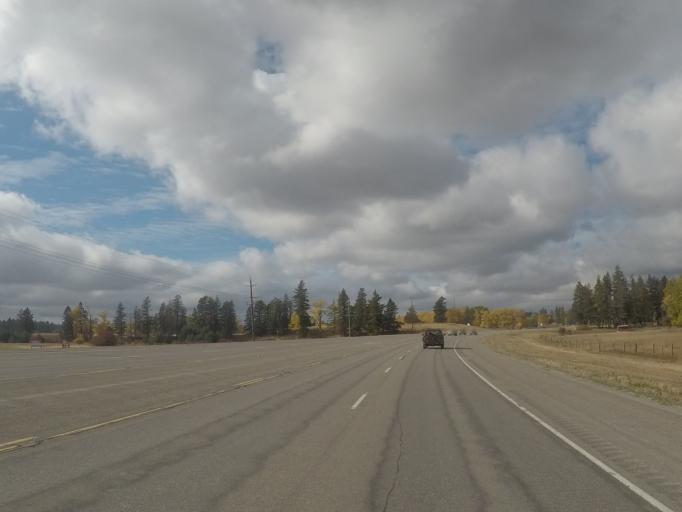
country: US
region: Montana
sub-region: Flathead County
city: Columbia Falls
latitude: 48.3637
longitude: -114.1598
